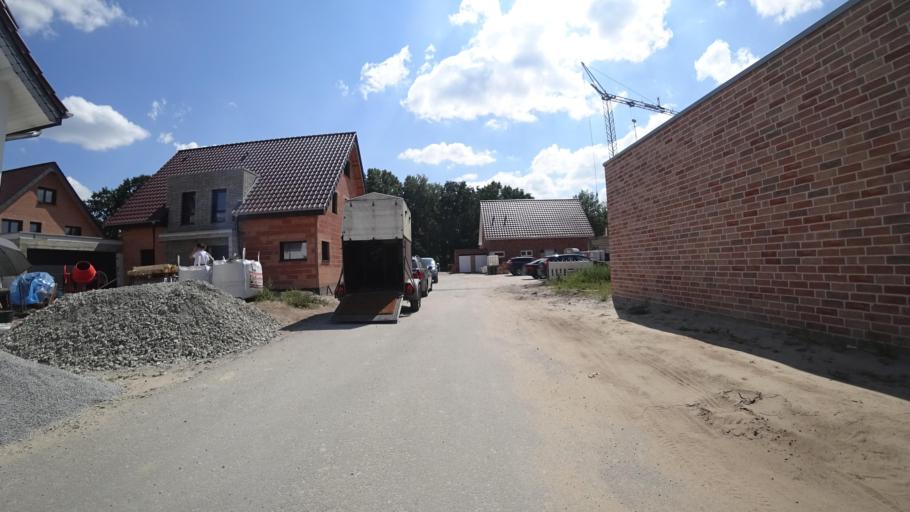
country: DE
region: North Rhine-Westphalia
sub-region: Regierungsbezirk Detmold
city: Guetersloh
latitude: 51.9294
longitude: 8.3924
